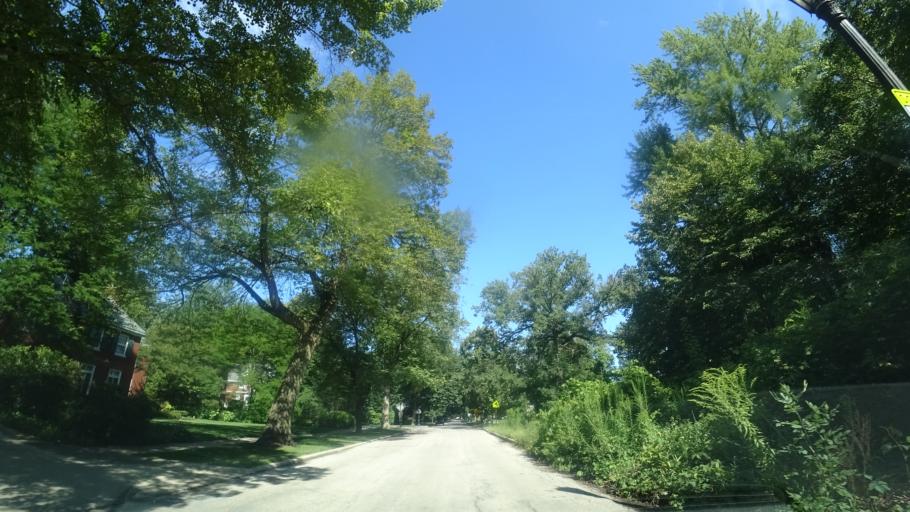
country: US
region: Illinois
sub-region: Cook County
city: Wilmette
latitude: 42.0607
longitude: -87.7115
